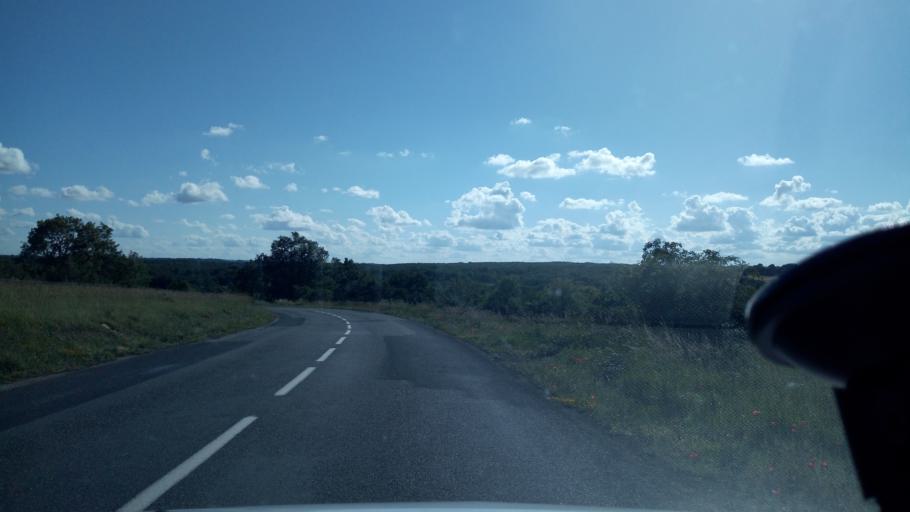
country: FR
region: Midi-Pyrenees
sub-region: Departement de l'Aveyron
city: Sebazac-Concoures
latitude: 44.4400
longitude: 2.6212
